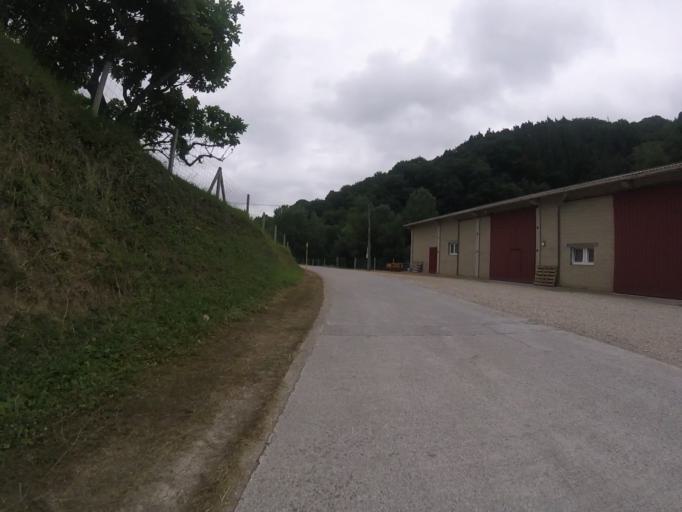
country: ES
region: Navarre
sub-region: Provincia de Navarra
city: Sunbilla
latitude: 43.1769
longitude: -1.6674
